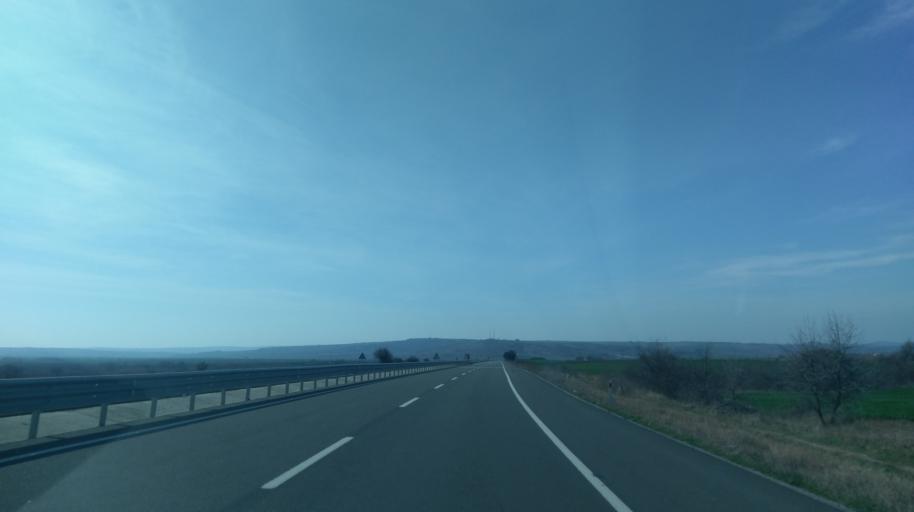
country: TR
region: Edirne
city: Hamidiye
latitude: 41.1304
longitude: 26.6585
